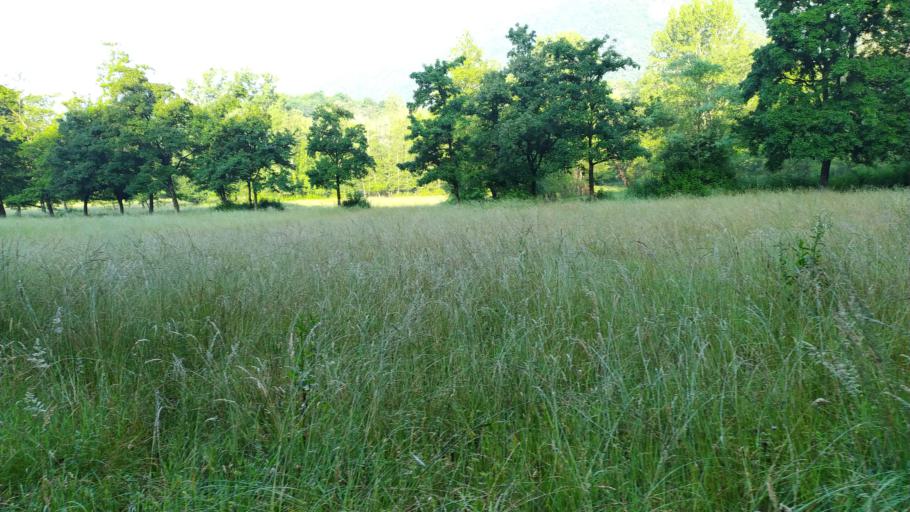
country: IT
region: Friuli Venezia Giulia
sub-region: Provincia di Pordenone
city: Polcenigo
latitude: 46.0233
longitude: 12.4957
